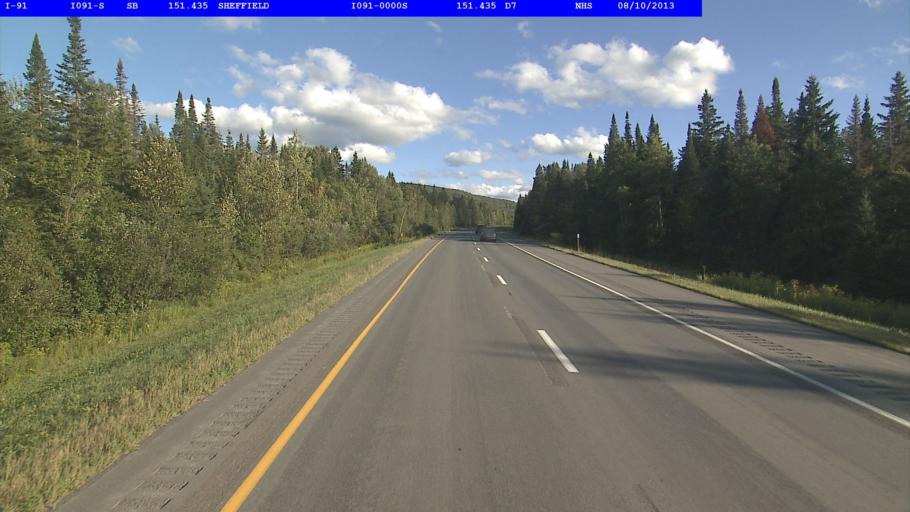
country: US
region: Vermont
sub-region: Caledonia County
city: Lyndonville
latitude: 44.6853
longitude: -72.1351
